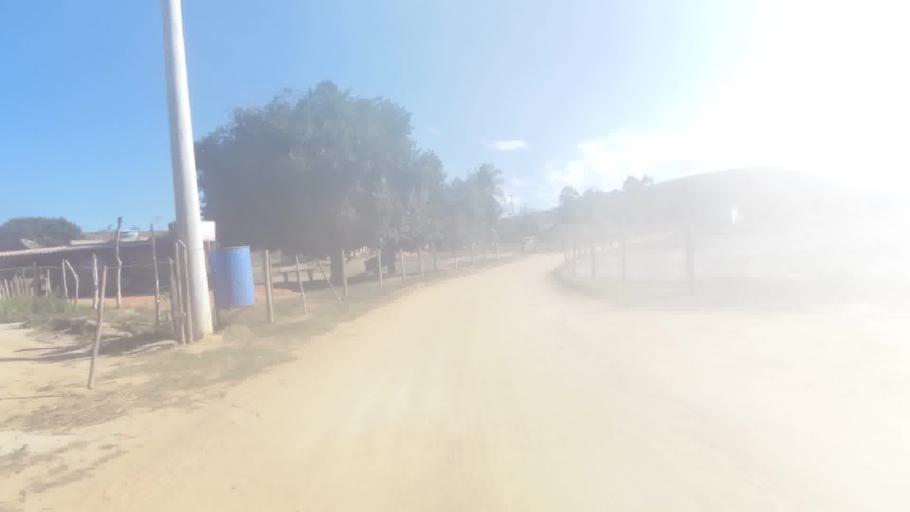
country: BR
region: Espirito Santo
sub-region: Cachoeiro De Itapemirim
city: Cachoeiro de Itapemirim
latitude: -21.0186
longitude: -41.0392
